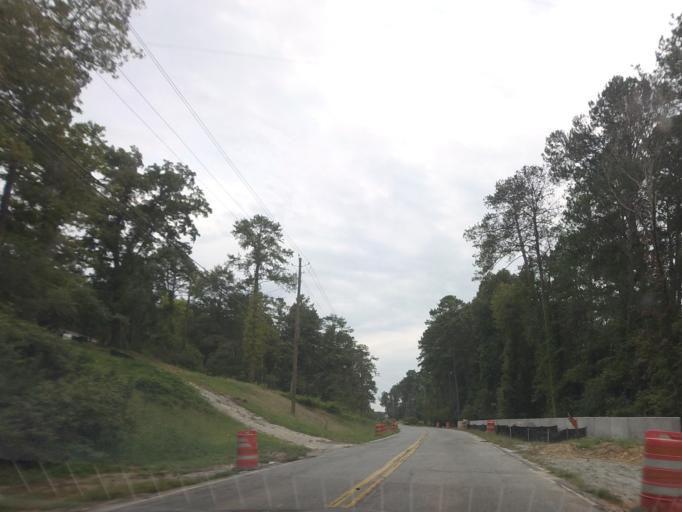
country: US
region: Georgia
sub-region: Bibb County
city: Macon
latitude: 32.8824
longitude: -83.6952
